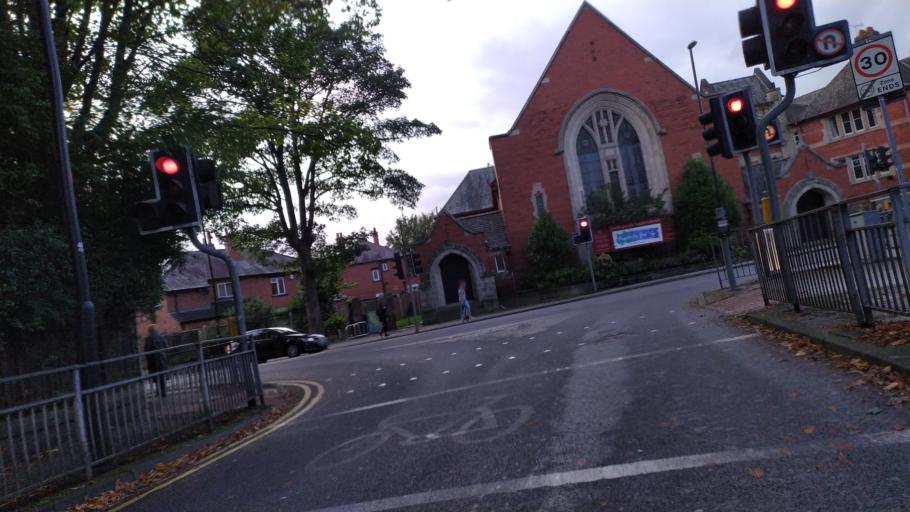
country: GB
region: England
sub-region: City and Borough of Leeds
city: Leeds
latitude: 53.8191
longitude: -1.5815
